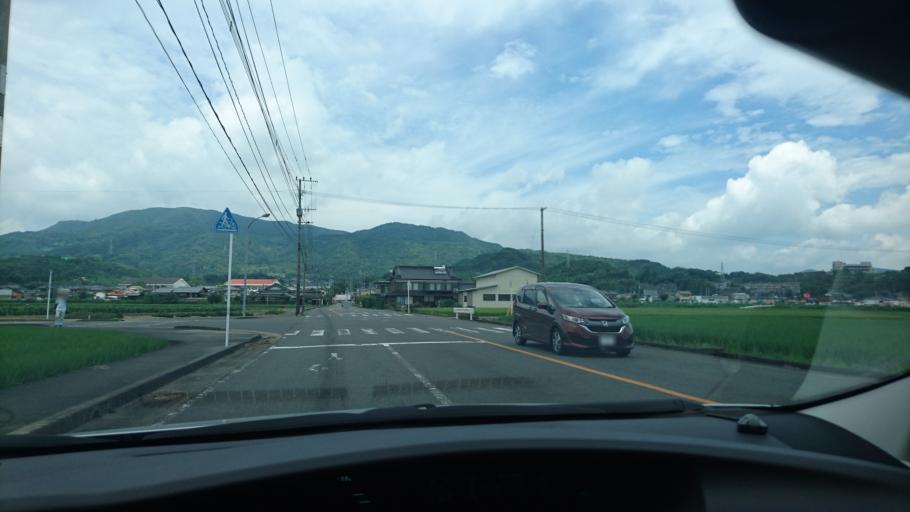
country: JP
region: Saga Prefecture
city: Takeocho-takeo
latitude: 33.2100
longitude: 130.1212
